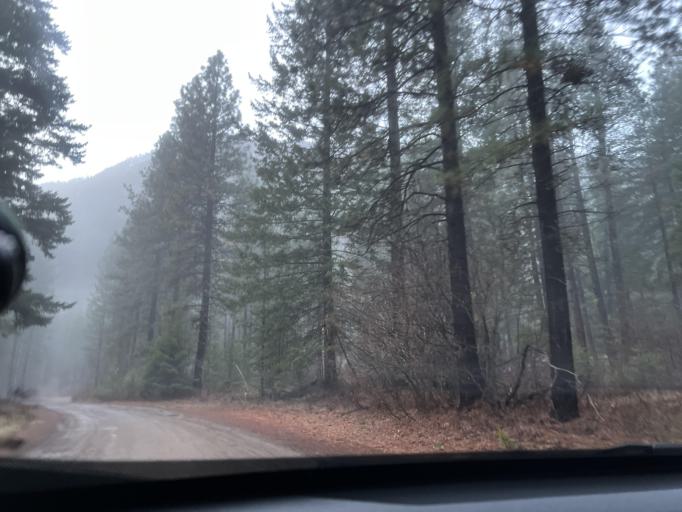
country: US
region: Washington
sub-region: Chelan County
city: Granite Falls
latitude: 48.5588
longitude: -120.3672
